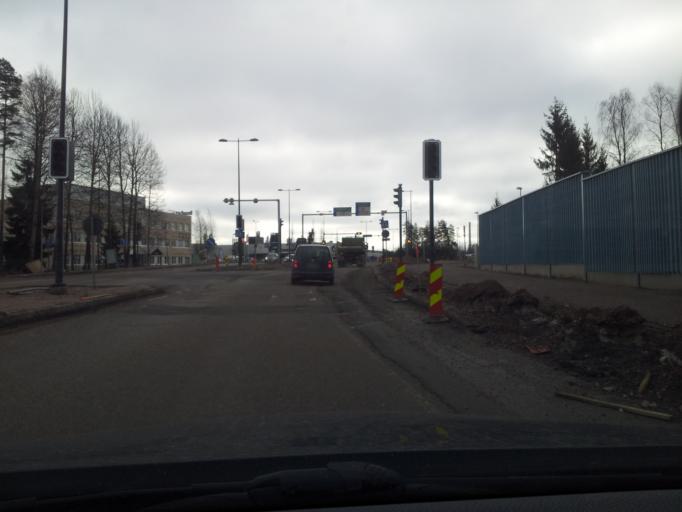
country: FI
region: Uusimaa
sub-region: Helsinki
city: Kauniainen
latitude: 60.1658
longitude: 24.7013
